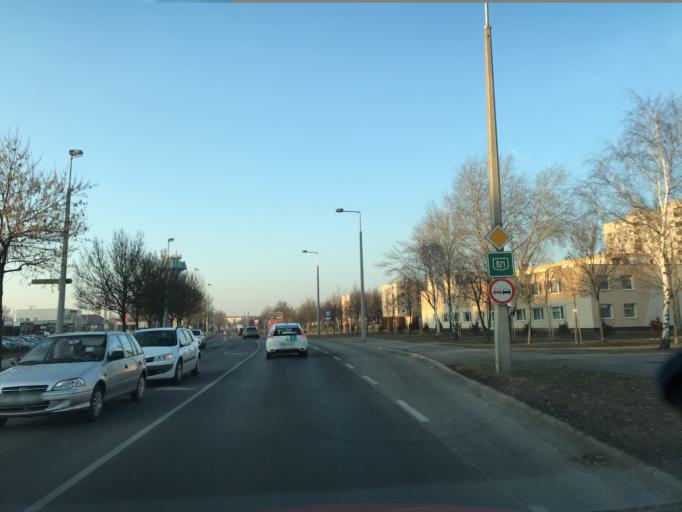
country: HU
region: Gyor-Moson-Sopron
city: Gyor
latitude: 47.6670
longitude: 17.6357
